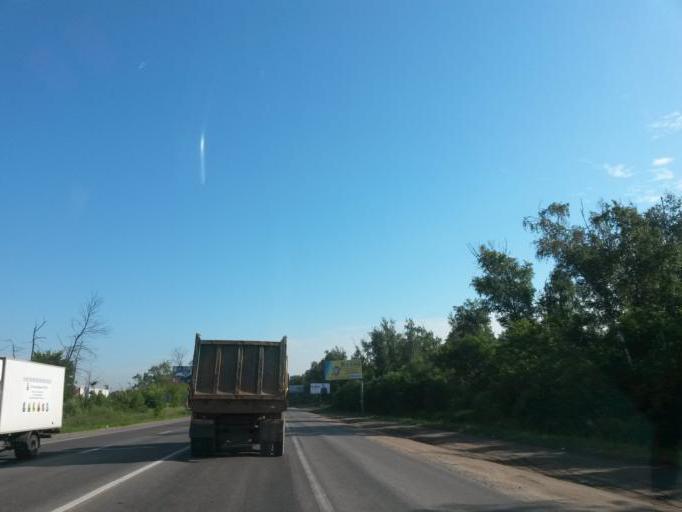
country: RU
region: Moskovskaya
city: Petrovskaya
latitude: 55.5536
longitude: 37.7750
